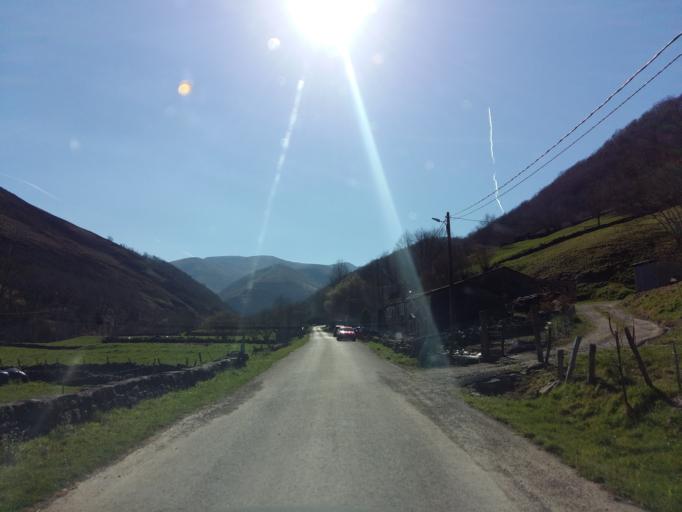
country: ES
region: Cantabria
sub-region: Provincia de Cantabria
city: Vega de Pas
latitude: 43.1450
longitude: -3.7985
